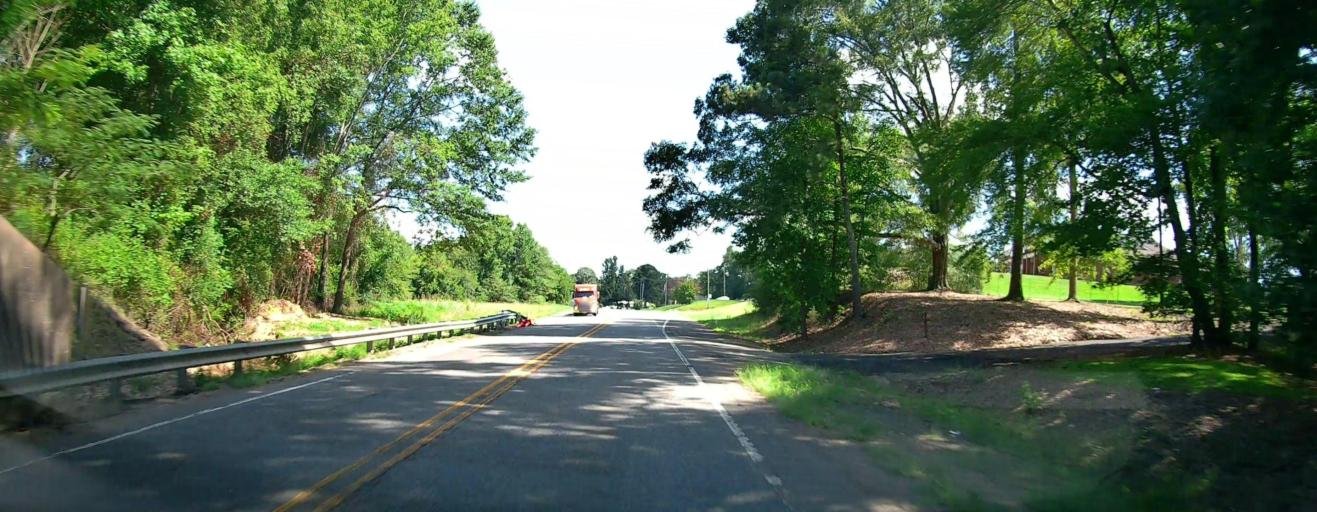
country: US
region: Alabama
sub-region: Pickens County
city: Gordo
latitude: 33.3238
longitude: -87.9103
